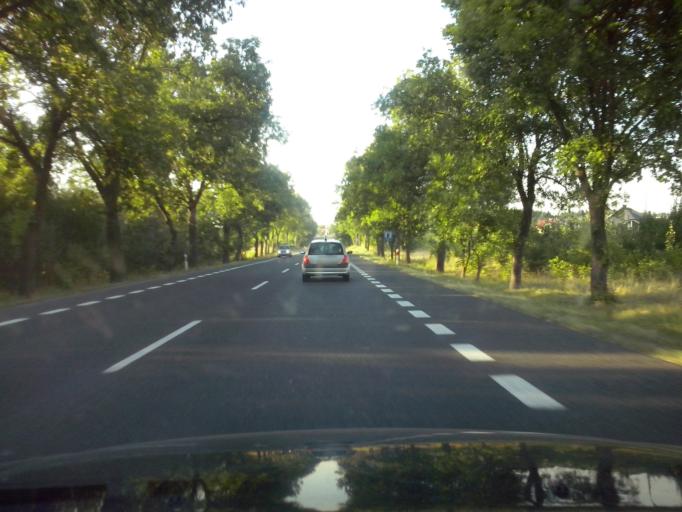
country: PL
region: Swietokrzyskie
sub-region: Powiat kielecki
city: Chmielnik
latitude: 50.6193
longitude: 20.7441
